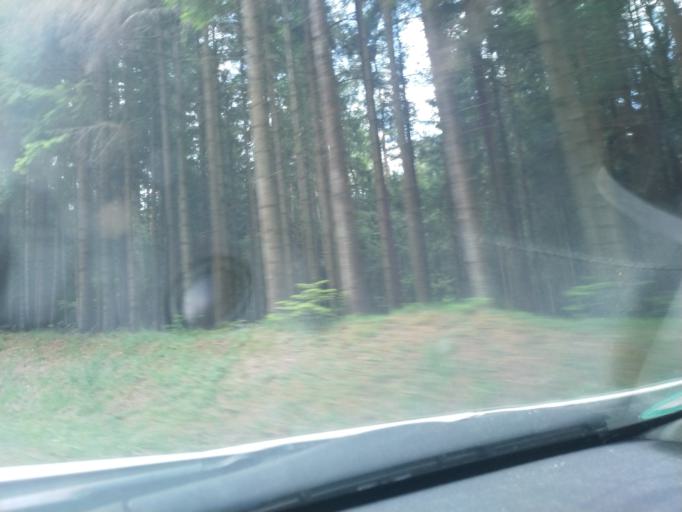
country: DE
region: Baden-Wuerttemberg
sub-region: Karlsruhe Region
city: Baiersbronn
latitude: 48.5804
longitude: 8.4216
